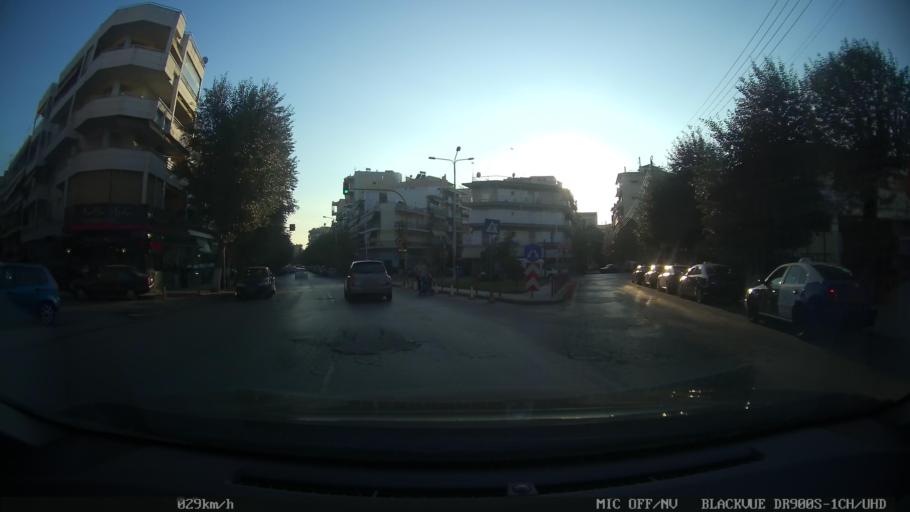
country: GR
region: Central Macedonia
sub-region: Nomos Thessalonikis
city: Triandria
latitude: 40.6079
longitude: 22.9763
